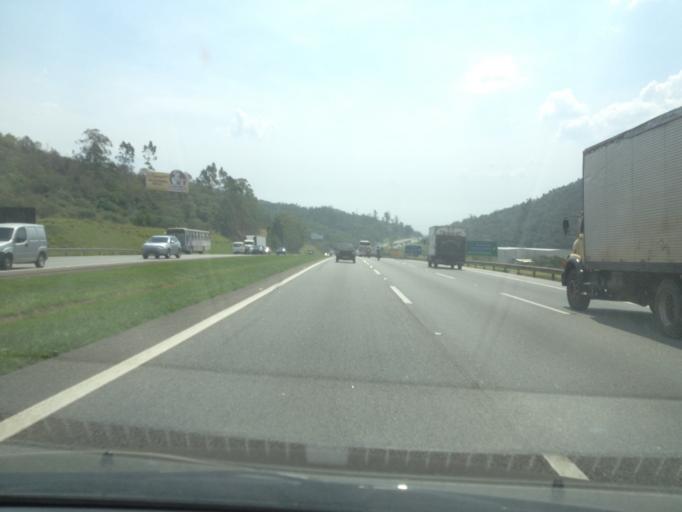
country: BR
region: Sao Paulo
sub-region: Pirapora Do Bom Jesus
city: Pirapora do Bom Jesus
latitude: -23.4699
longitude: -47.0153
